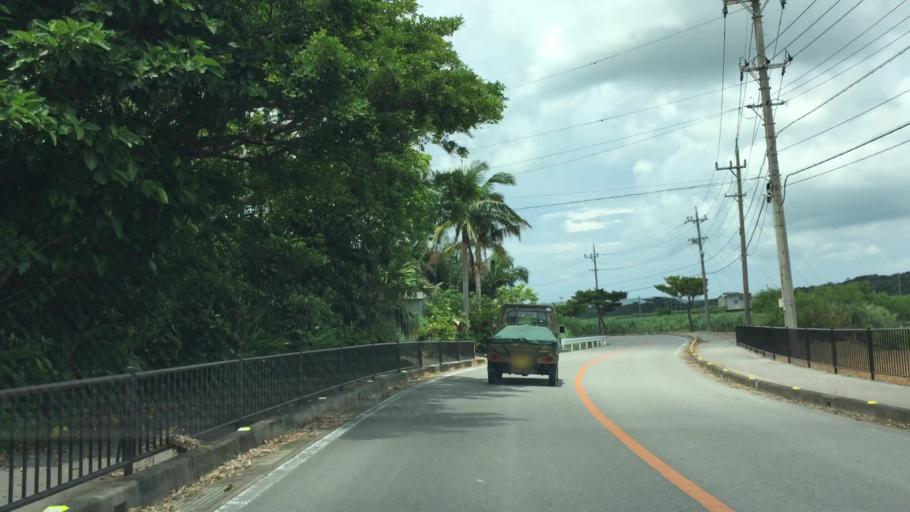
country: JP
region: Okinawa
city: Ishigaki
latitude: 24.3972
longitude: 124.1552
